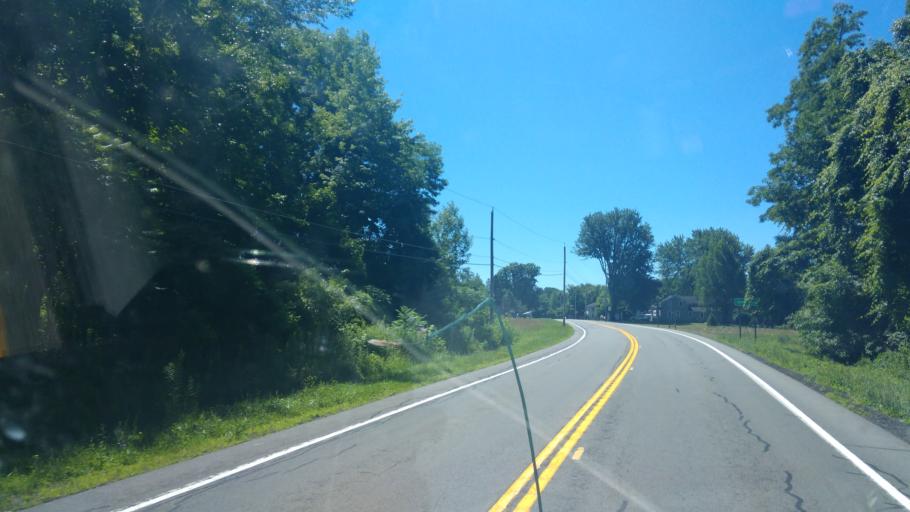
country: US
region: New York
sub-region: Wayne County
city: Sodus
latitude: 43.1706
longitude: -76.9878
